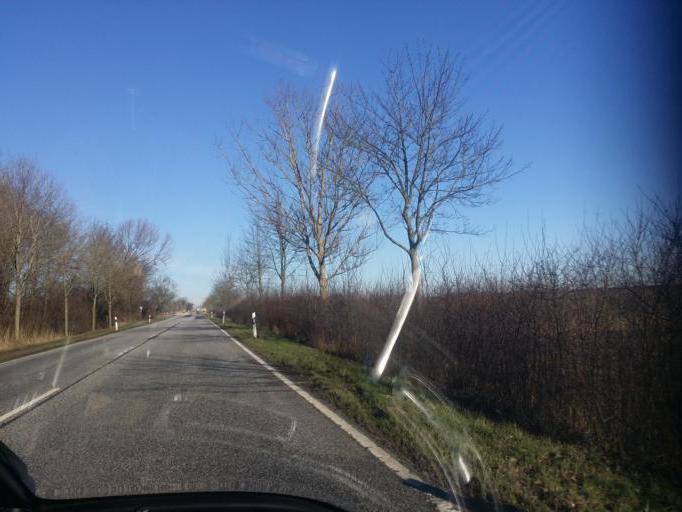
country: DE
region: Schleswig-Holstein
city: Oldenswort
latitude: 54.3627
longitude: 8.9759
